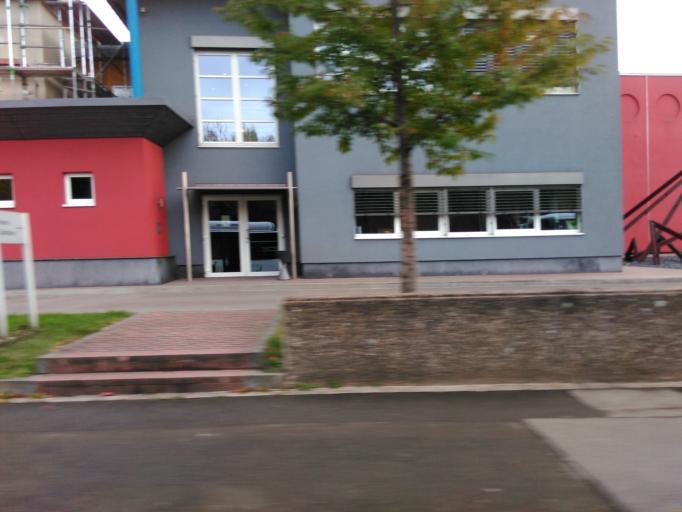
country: LU
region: Luxembourg
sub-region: Canton d'Esch-sur-Alzette
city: Esch-sur-Alzette
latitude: 49.5060
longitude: 5.9598
